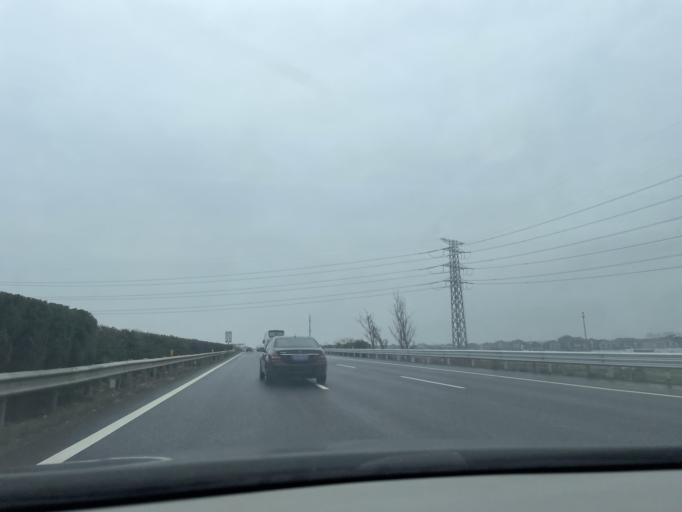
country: CN
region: Zhejiang Sheng
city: Liutangting
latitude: 30.2747
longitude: 121.3081
